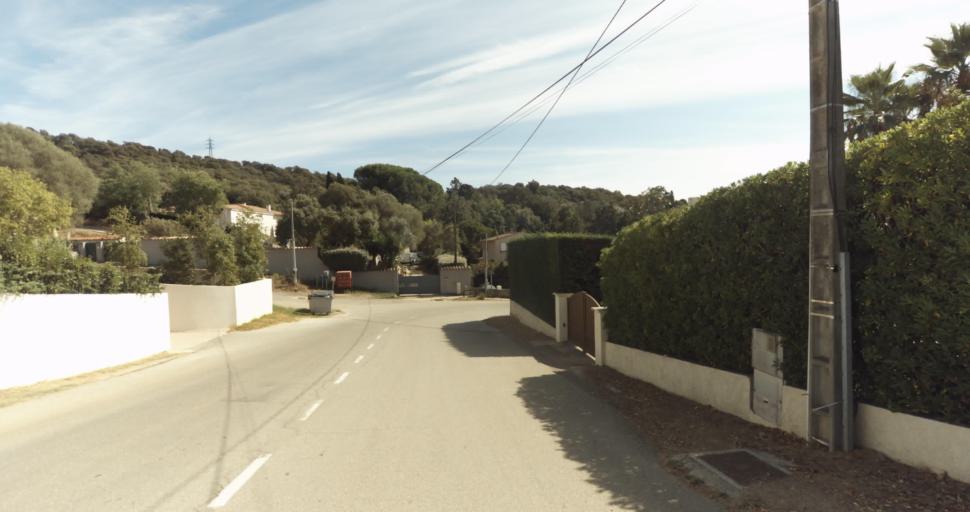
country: FR
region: Corsica
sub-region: Departement de la Corse-du-Sud
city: Ajaccio
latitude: 41.9408
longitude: 8.7646
